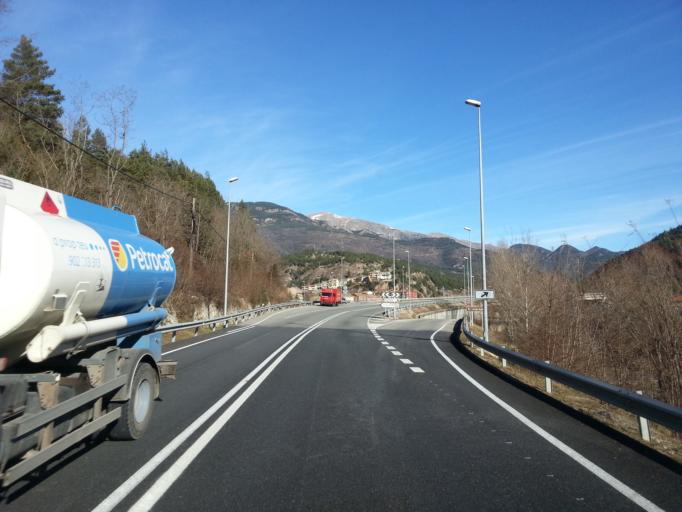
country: ES
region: Catalonia
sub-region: Provincia de Barcelona
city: Guardiola de Bergueda
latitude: 42.2268
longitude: 1.8749
